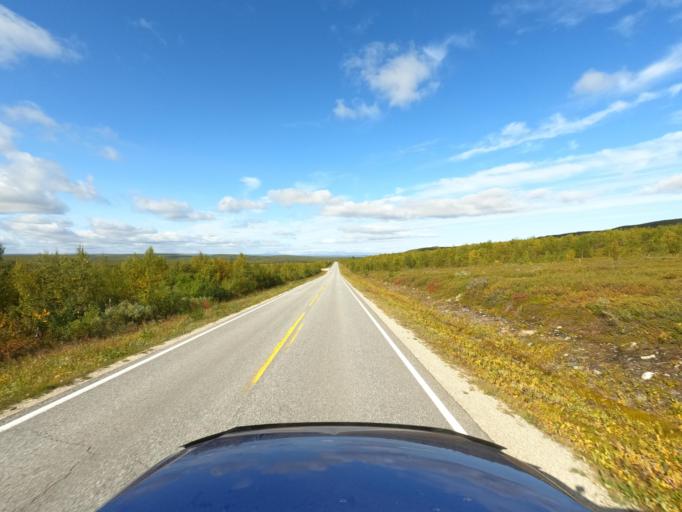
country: NO
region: Finnmark Fylke
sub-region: Karasjok
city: Karasjohka
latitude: 69.5595
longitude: 25.3928
